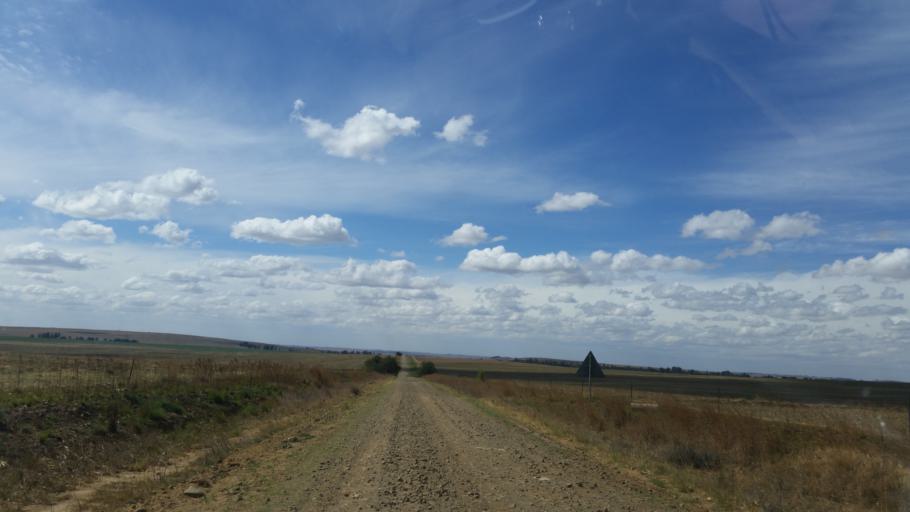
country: ZA
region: Orange Free State
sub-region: Thabo Mofutsanyana District Municipality
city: Bethlehem
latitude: -28.2218
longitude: 28.4978
